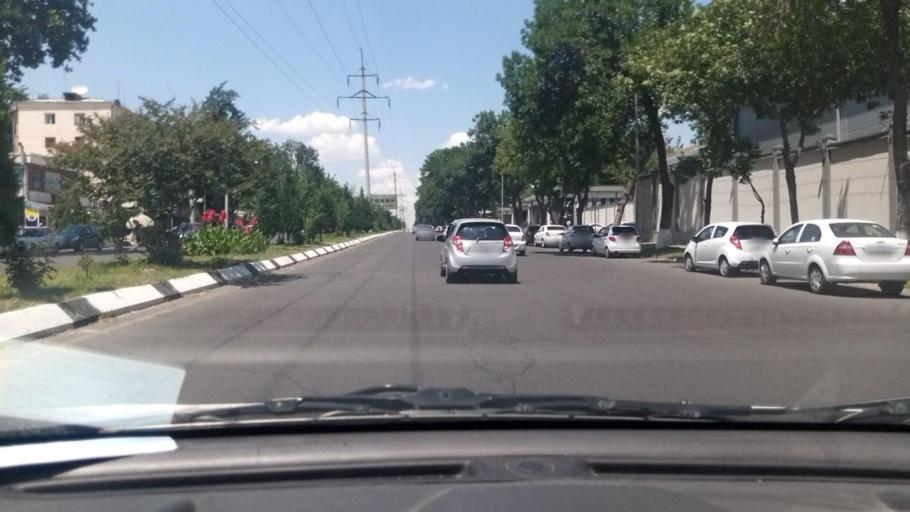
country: UZ
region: Toshkent Shahri
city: Tashkent
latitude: 41.2872
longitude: 69.1946
